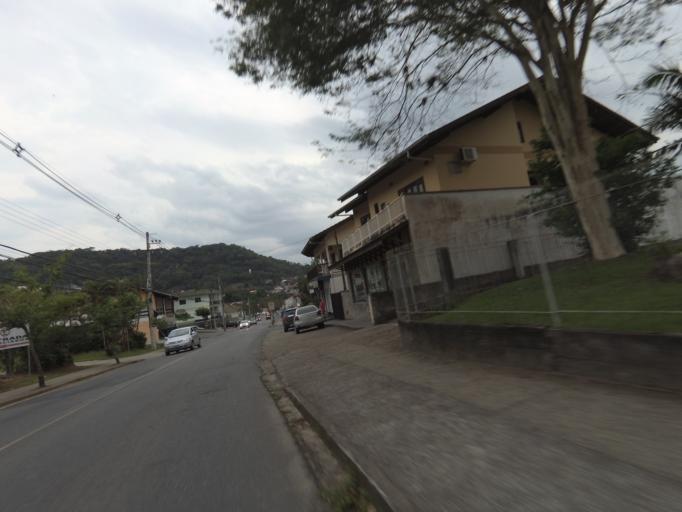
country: BR
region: Santa Catarina
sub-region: Blumenau
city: Blumenau
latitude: -26.8700
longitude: -49.0495
